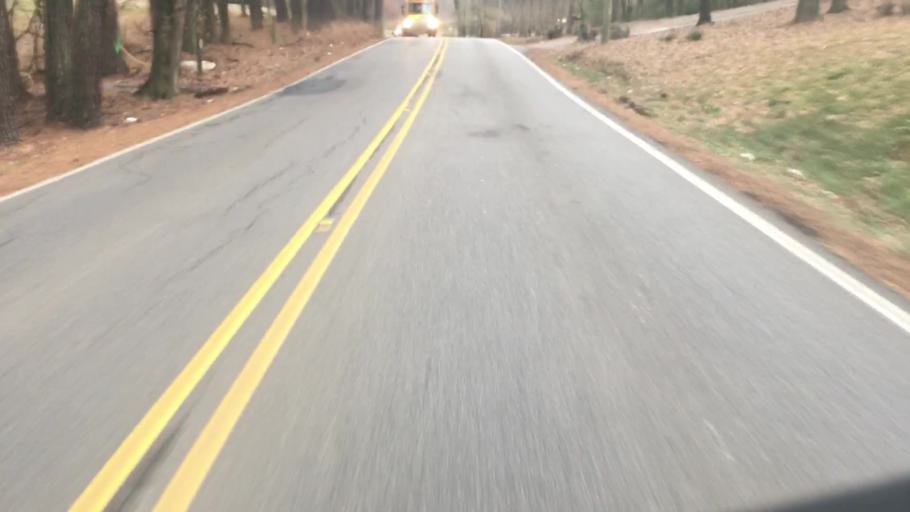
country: US
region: Alabama
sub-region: Jefferson County
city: Cahaba Heights
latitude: 33.4197
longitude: -86.7495
